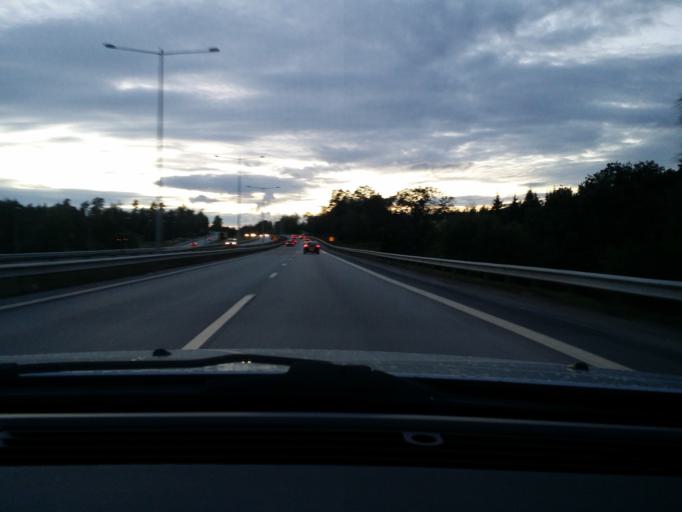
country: SE
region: Stockholm
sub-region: Upplands-Bro Kommun
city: Kungsaengen
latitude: 59.4800
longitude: 17.7853
